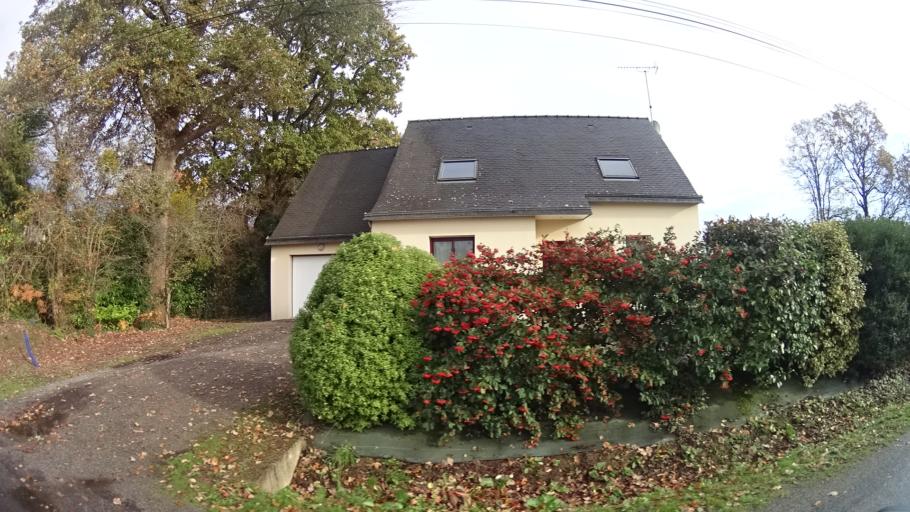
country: FR
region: Brittany
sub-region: Departement du Morbihan
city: Rieux
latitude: 47.6185
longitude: -2.1089
